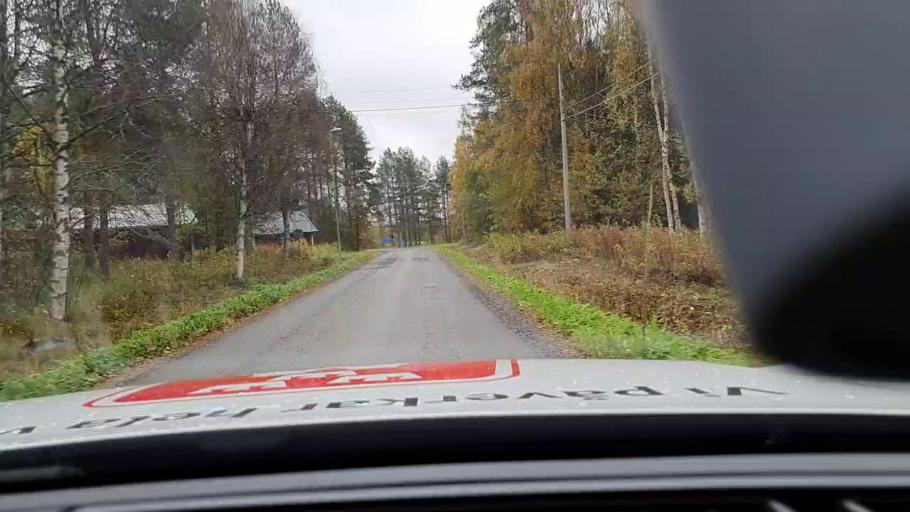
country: FI
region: Lapland
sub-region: Kemi-Tornio
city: Tornio
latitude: 65.9754
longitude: 24.0263
